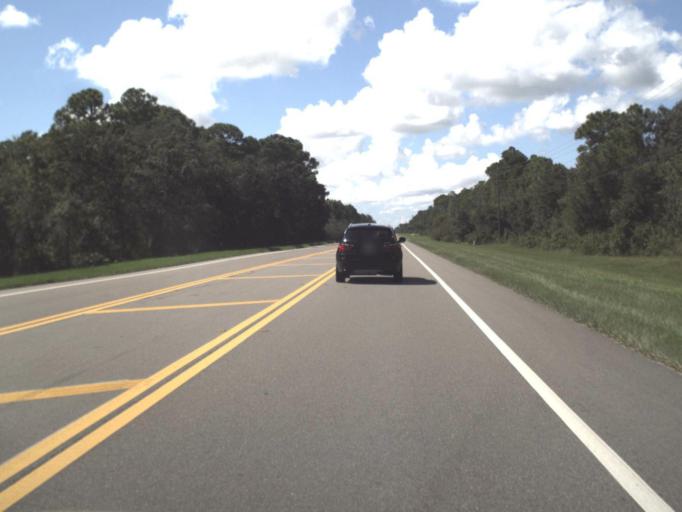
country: US
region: Florida
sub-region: Sarasota County
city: The Meadows
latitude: 27.4031
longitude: -82.3139
